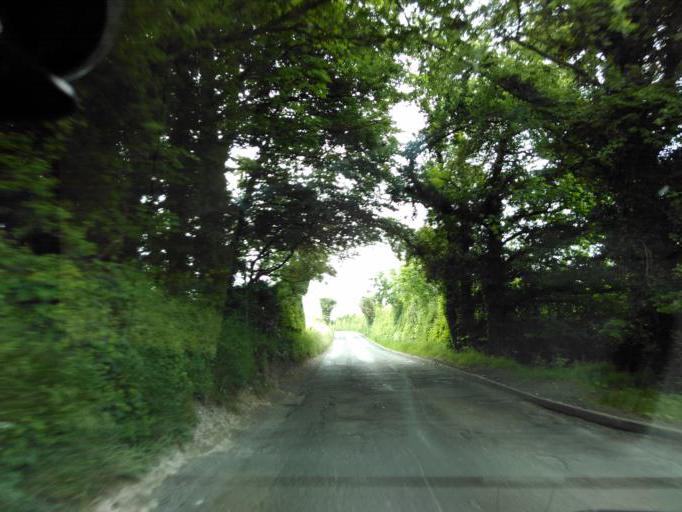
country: GB
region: England
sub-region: Kent
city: Chartham
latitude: 51.2402
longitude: 1.0409
